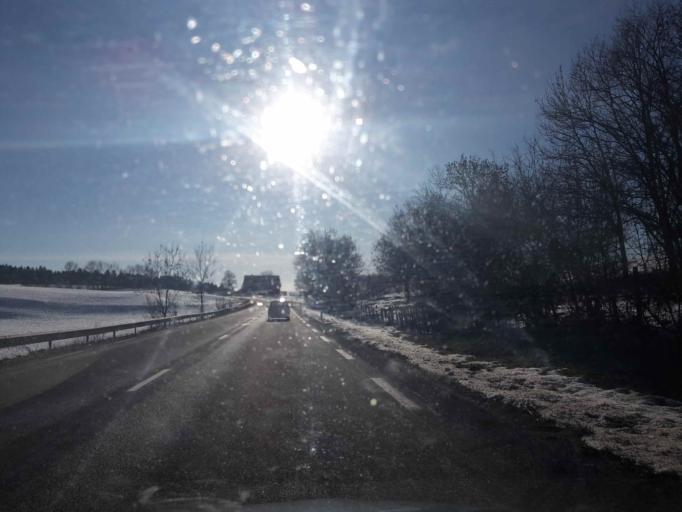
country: FR
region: Franche-Comte
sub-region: Departement du Doubs
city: Doubs
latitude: 47.0362
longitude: 6.3378
